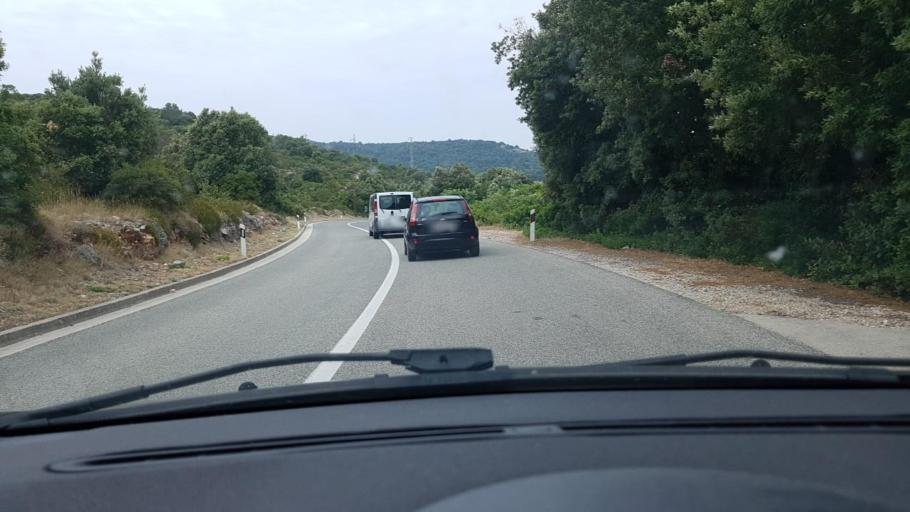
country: HR
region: Dubrovacko-Neretvanska
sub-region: Grad Korcula
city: Zrnovo
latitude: 42.9447
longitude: 17.0481
